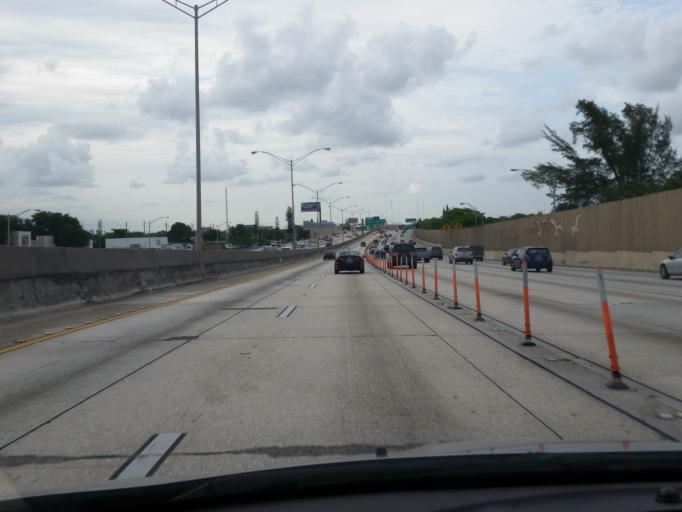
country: US
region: Florida
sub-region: Miami-Dade County
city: Golden Glades
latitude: 25.9002
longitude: -80.2098
